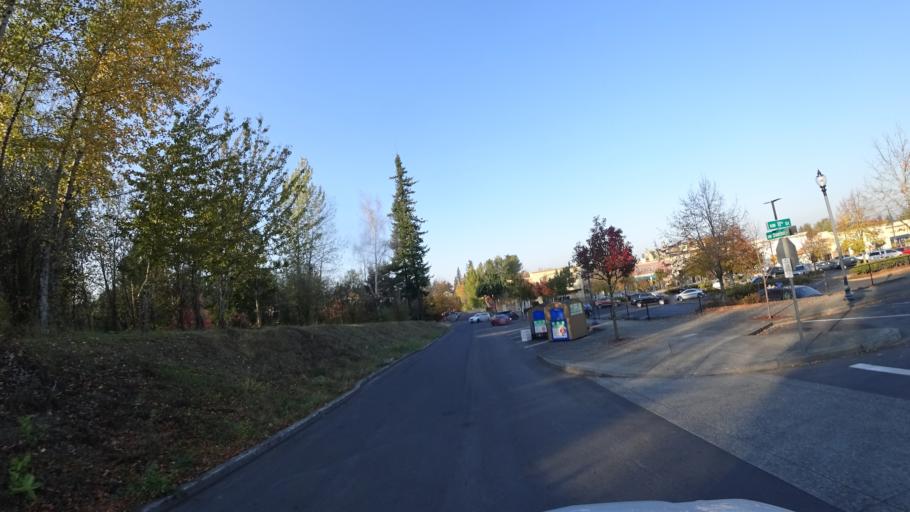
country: US
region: Oregon
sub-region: Multnomah County
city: Gresham
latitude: 45.5051
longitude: -122.4425
